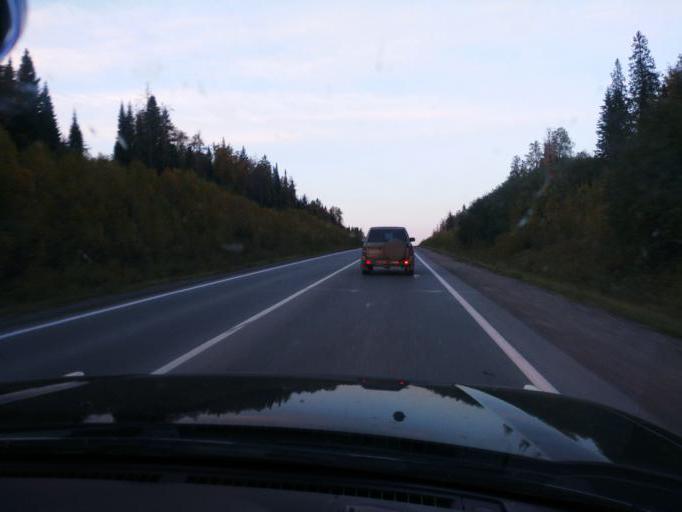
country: RU
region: Perm
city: Sylva
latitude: 58.2861
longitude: 56.7397
